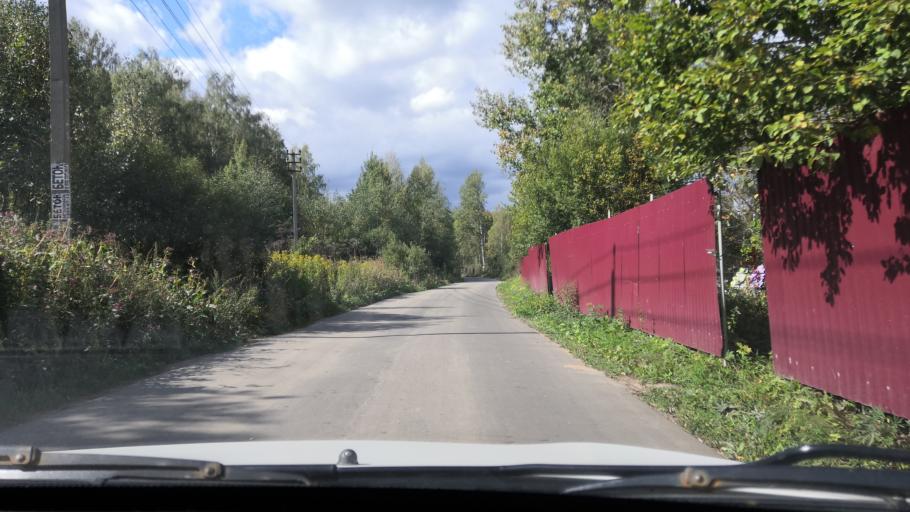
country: RU
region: Moskovskaya
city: Povarovo
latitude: 56.0646
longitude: 37.0389
